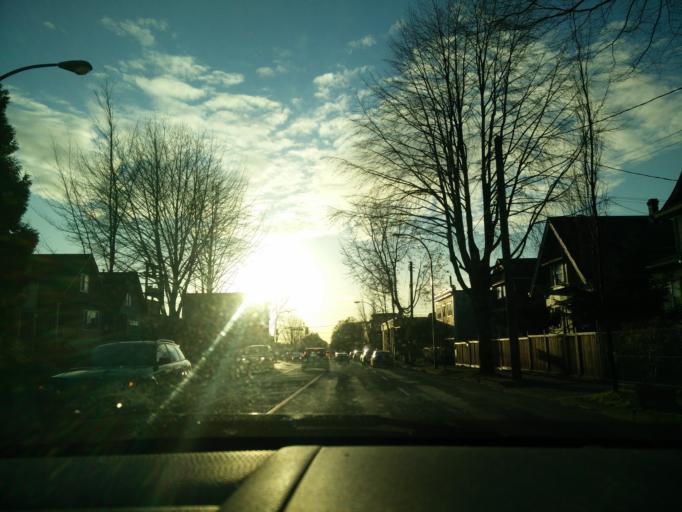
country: CA
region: British Columbia
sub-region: Fraser Valley Regional District
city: North Vancouver
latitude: 49.2697
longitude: -123.0678
